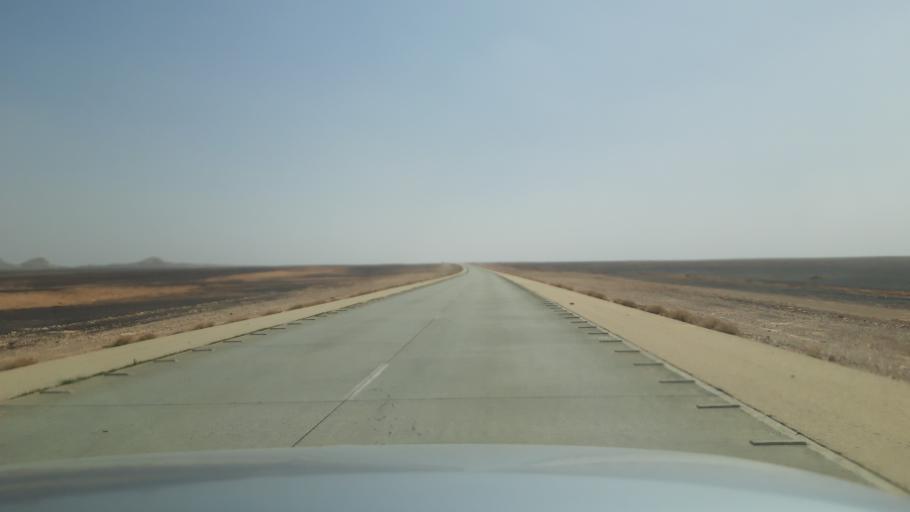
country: SA
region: Al Jawf
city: Al Qurayyat
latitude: 31.0158
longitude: 36.6336
